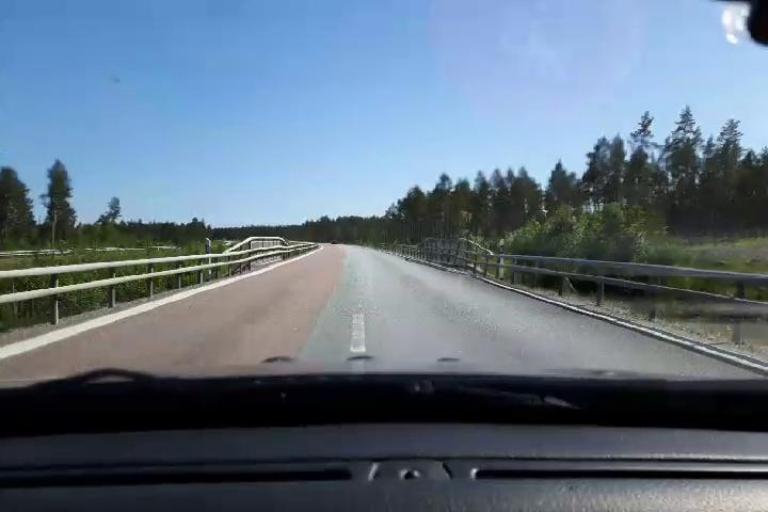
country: SE
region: Gaevleborg
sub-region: Soderhamns Kommun
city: Soderhamn
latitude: 61.3809
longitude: 16.9932
